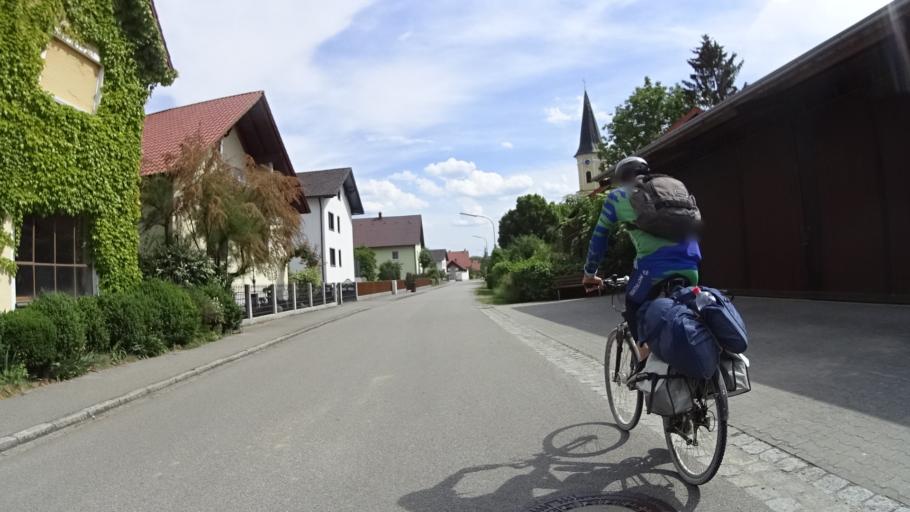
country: DE
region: Bavaria
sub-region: Upper Palatinate
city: Wiesent
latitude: 48.9946
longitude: 12.3484
